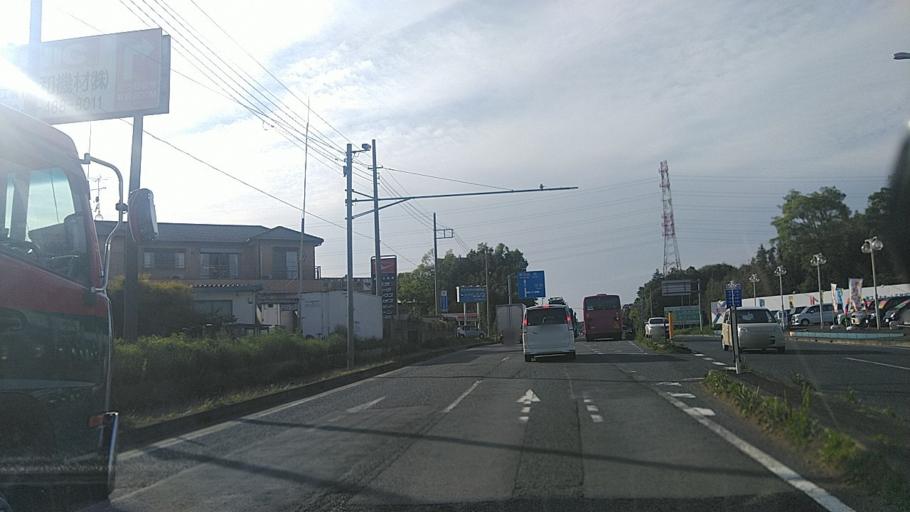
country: JP
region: Chiba
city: Shiroi
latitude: 35.7639
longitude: 140.1028
